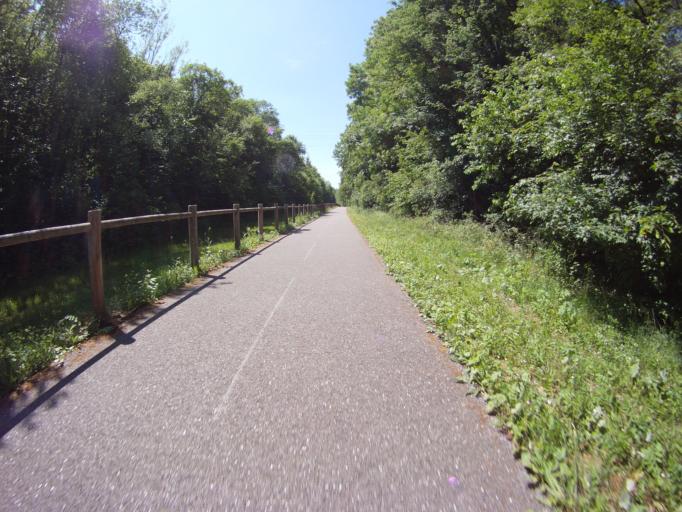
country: FR
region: Lorraine
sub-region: Departement de Meurthe-et-Moselle
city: Champenoux
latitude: 48.7467
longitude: 6.3216
